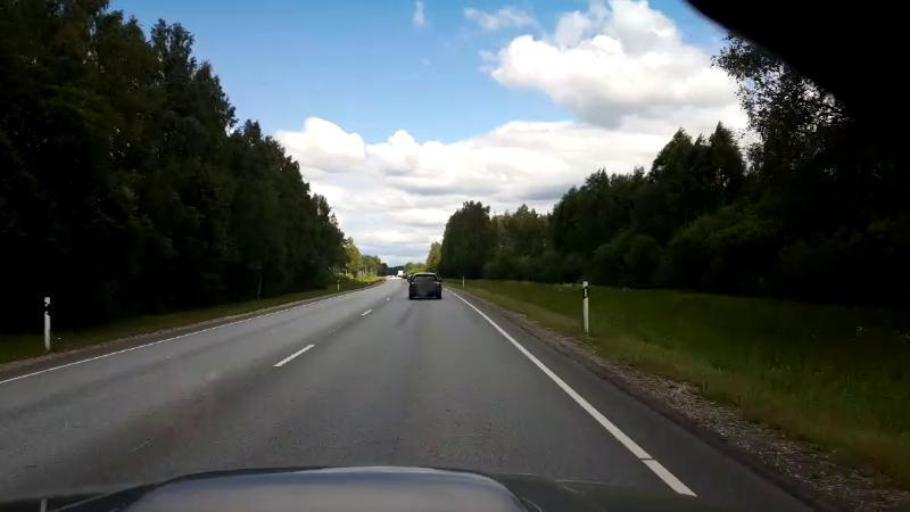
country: EE
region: Paernumaa
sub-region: Sauga vald
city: Sauga
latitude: 58.4581
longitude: 24.5131
